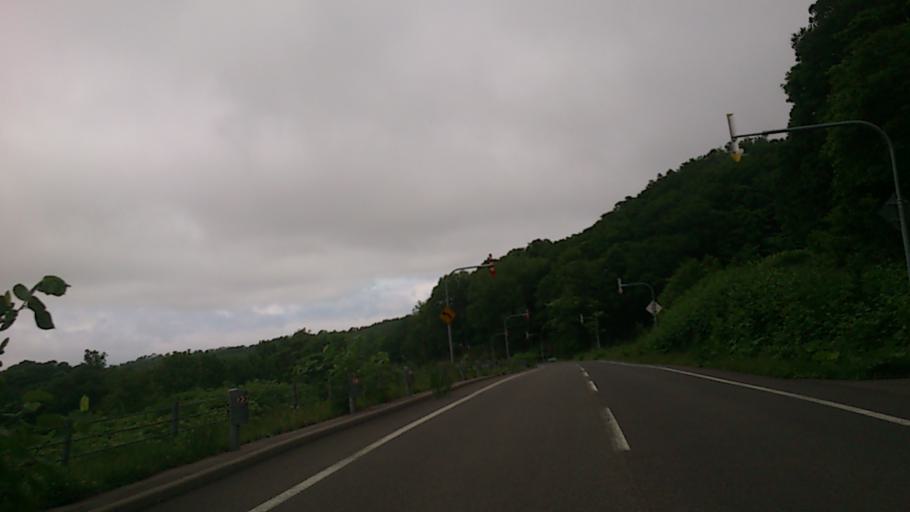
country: JP
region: Hokkaido
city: Niseko Town
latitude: 42.8562
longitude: 140.5871
